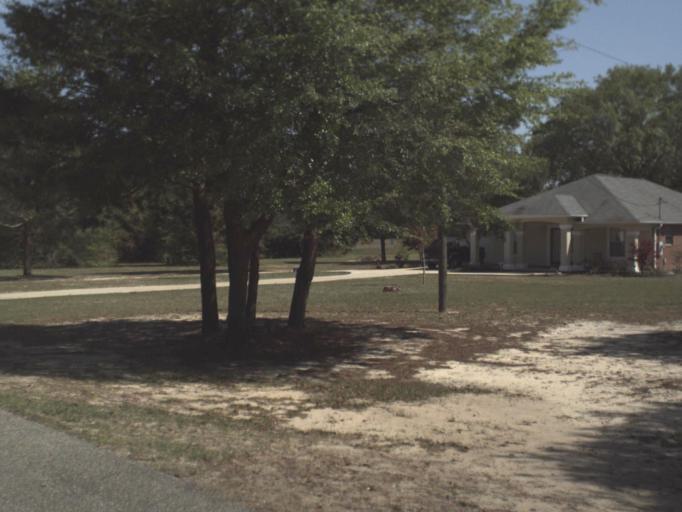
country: US
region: Florida
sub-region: Okaloosa County
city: Crestview
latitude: 30.7512
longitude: -86.4831
